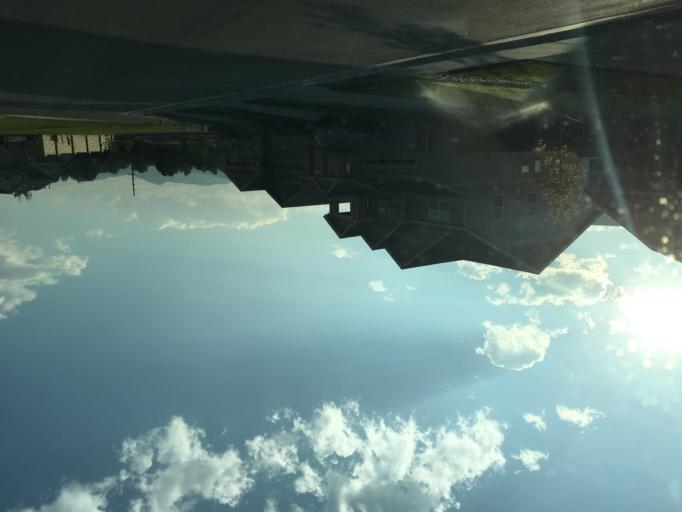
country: US
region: Colorado
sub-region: Jefferson County
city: Applewood
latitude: 39.7844
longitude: -105.1735
